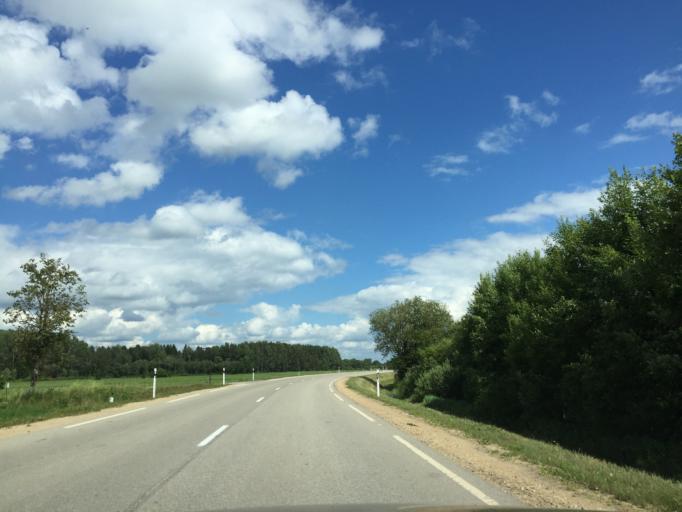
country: LV
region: Malpils
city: Malpils
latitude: 56.8995
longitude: 24.9112
